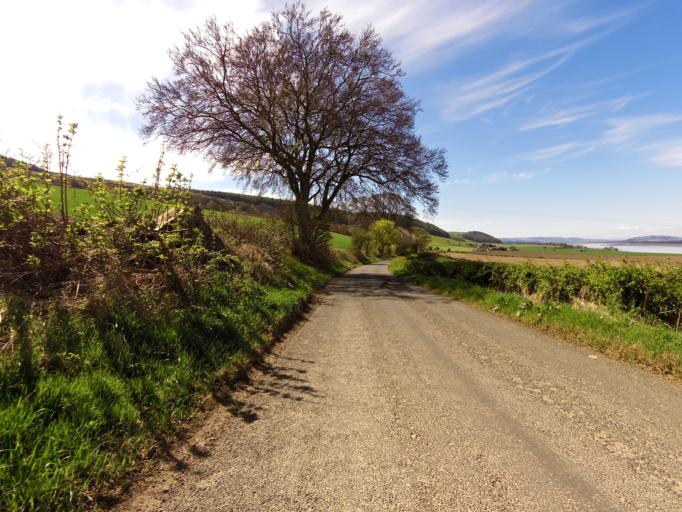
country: GB
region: Scotland
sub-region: Perth and Kinross
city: Errol
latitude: 56.3785
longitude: -3.1387
